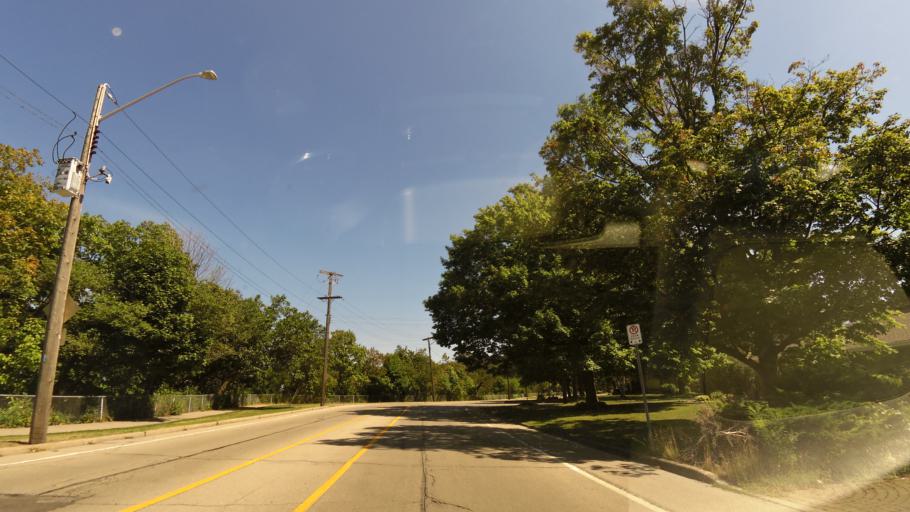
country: CA
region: Ontario
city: Hamilton
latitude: 43.2453
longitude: -79.9102
